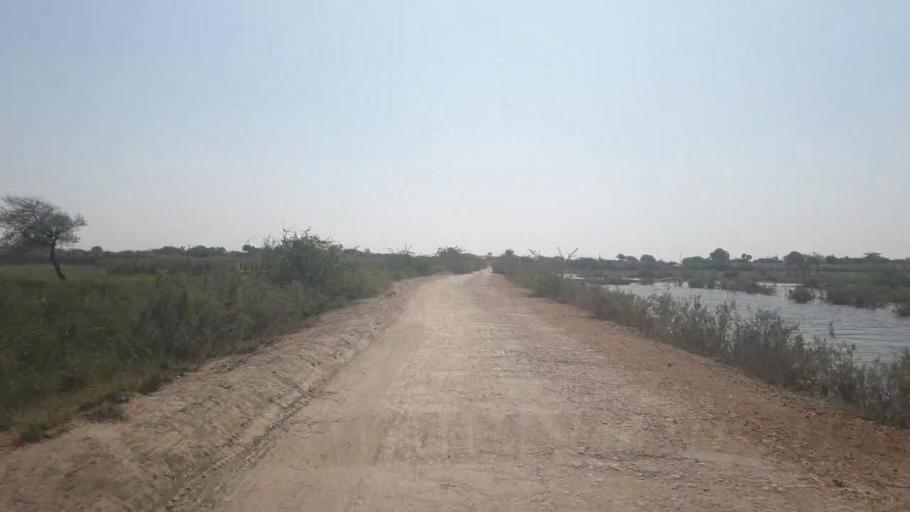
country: PK
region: Sindh
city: Badin
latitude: 24.6495
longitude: 68.9170
